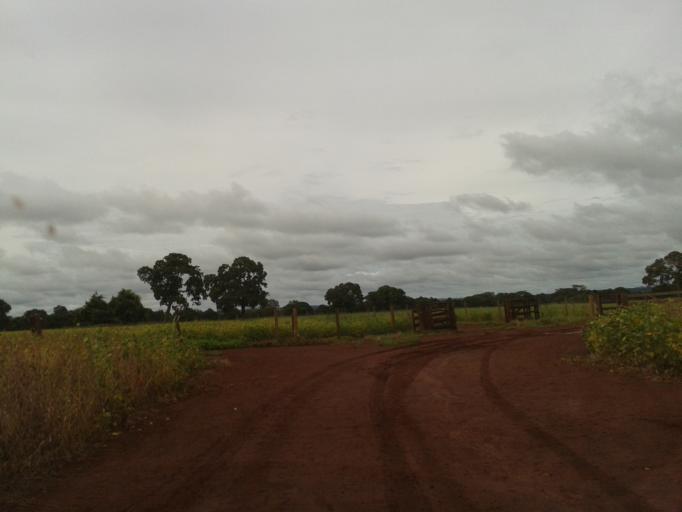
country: BR
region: Minas Gerais
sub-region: Capinopolis
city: Capinopolis
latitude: -18.7790
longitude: -49.7680
